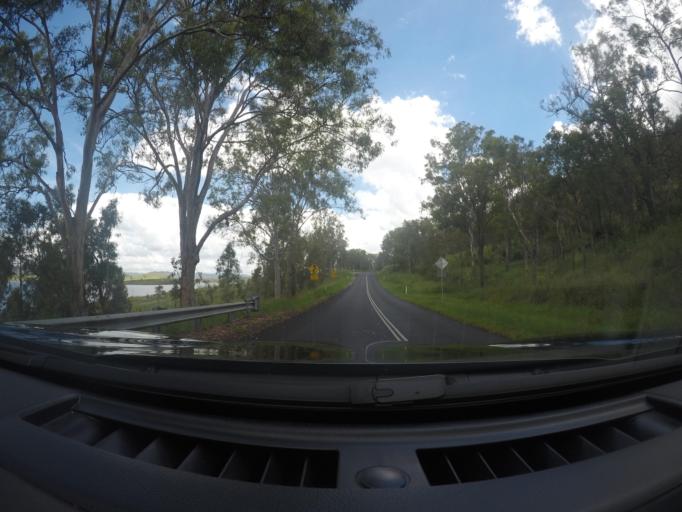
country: AU
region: Queensland
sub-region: Moreton Bay
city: Woodford
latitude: -27.0896
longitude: 152.5629
